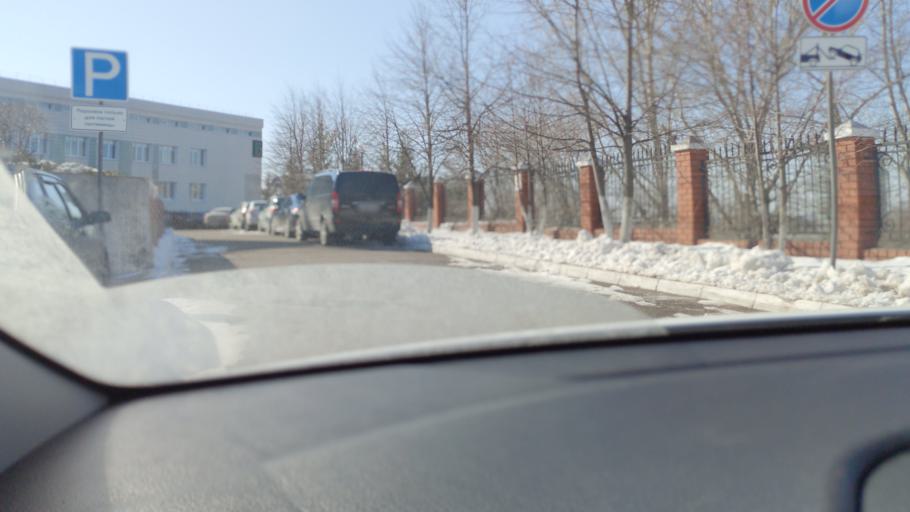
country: RU
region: Tatarstan
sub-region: Gorod Kazan'
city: Kazan
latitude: 55.7532
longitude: 49.1702
